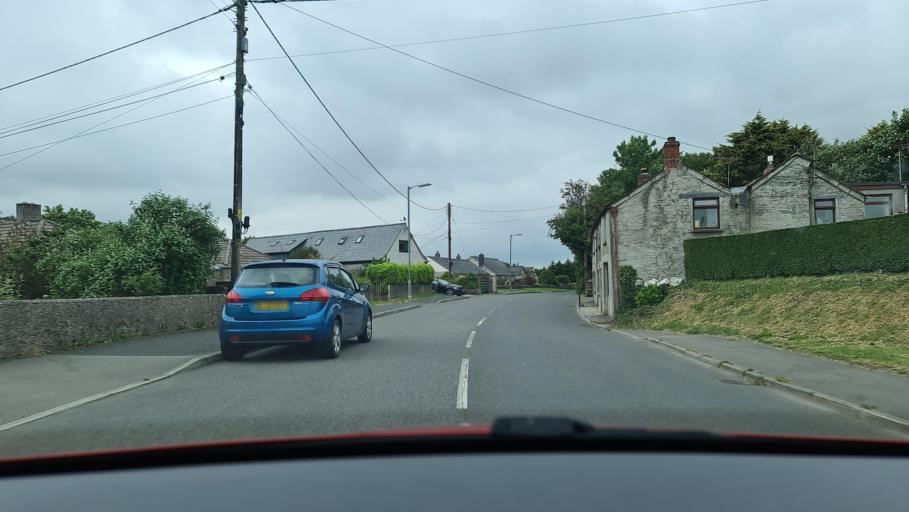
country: GB
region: England
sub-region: Cornwall
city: Camelford
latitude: 50.6205
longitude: -4.6824
